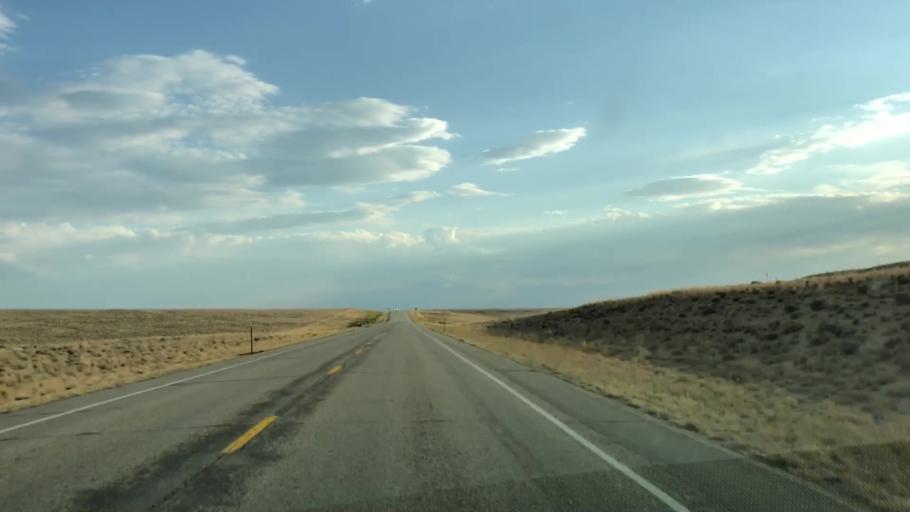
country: US
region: Wyoming
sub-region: Sweetwater County
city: North Rock Springs
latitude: 42.2071
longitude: -109.4747
